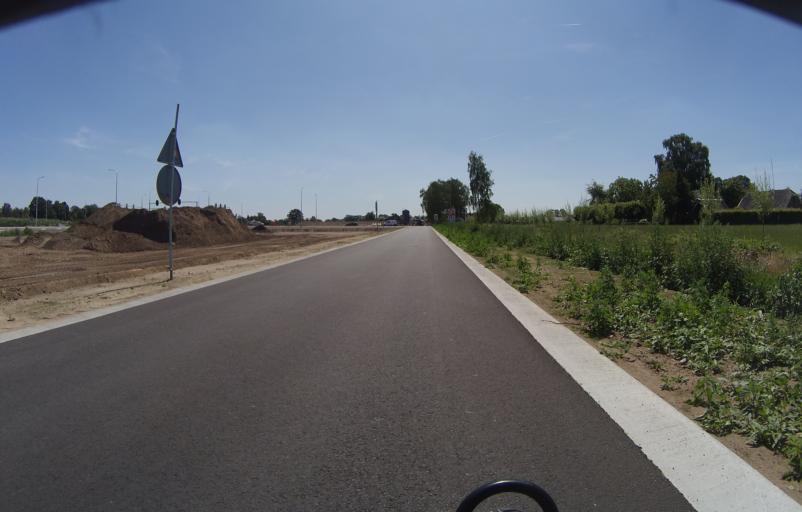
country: NL
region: Gelderland
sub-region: Gemeente Barneveld
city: Voorthuizen
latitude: 52.1800
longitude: 5.5837
